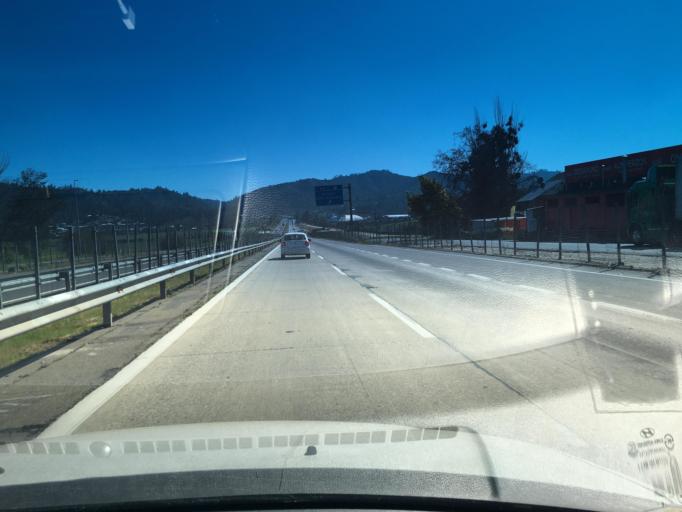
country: CL
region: Valparaiso
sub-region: Provincia de Marga Marga
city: Quilpue
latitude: -33.2569
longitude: -71.4395
